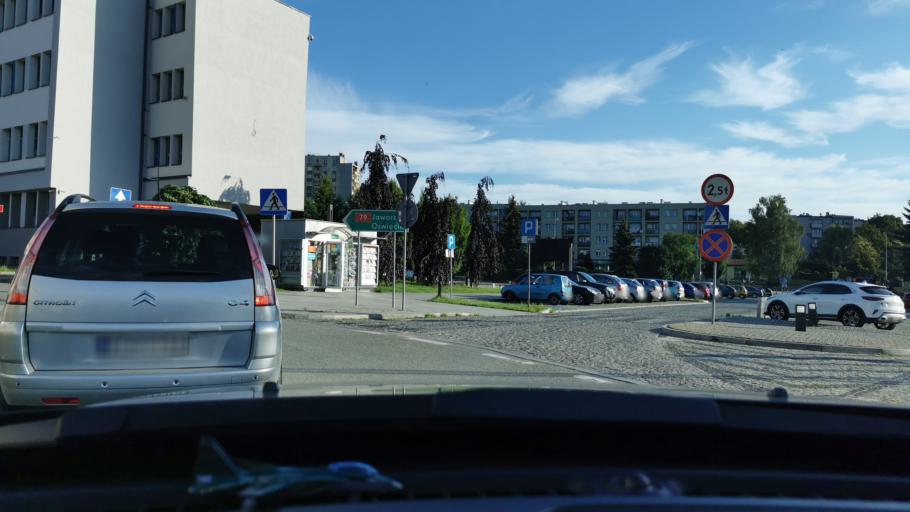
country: PL
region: Lesser Poland Voivodeship
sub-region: Powiat chrzanowski
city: Chrzanow
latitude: 50.1428
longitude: 19.4069
